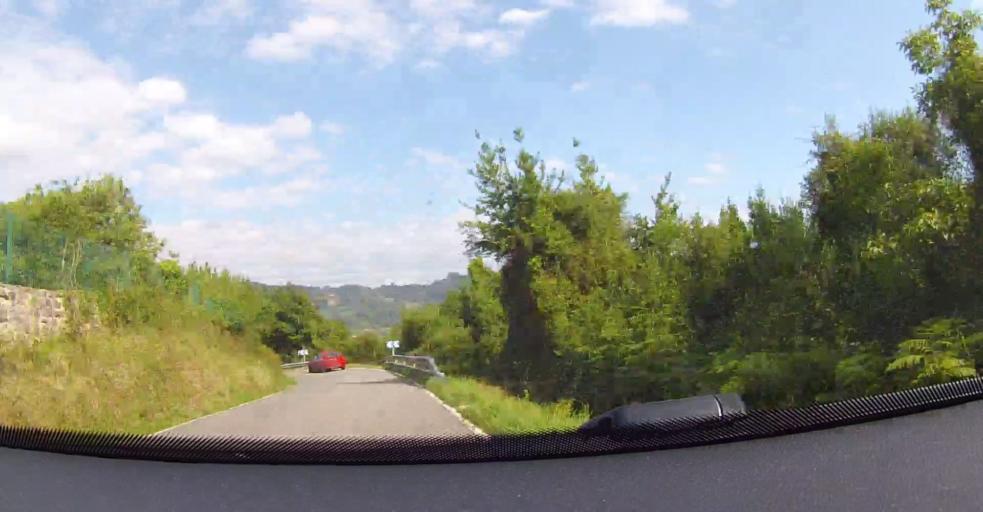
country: ES
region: Asturias
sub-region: Province of Asturias
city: Villaviciosa
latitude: 43.4861
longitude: -5.4199
